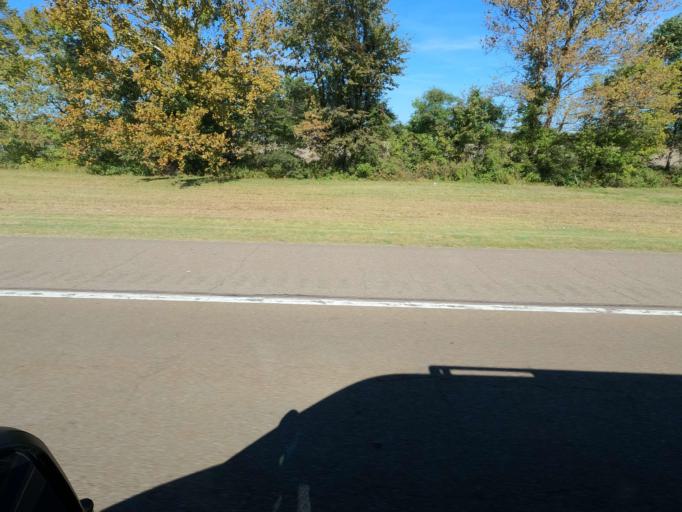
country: US
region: Tennessee
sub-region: Dyer County
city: Dyersburg
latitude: 36.0686
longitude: -89.3788
